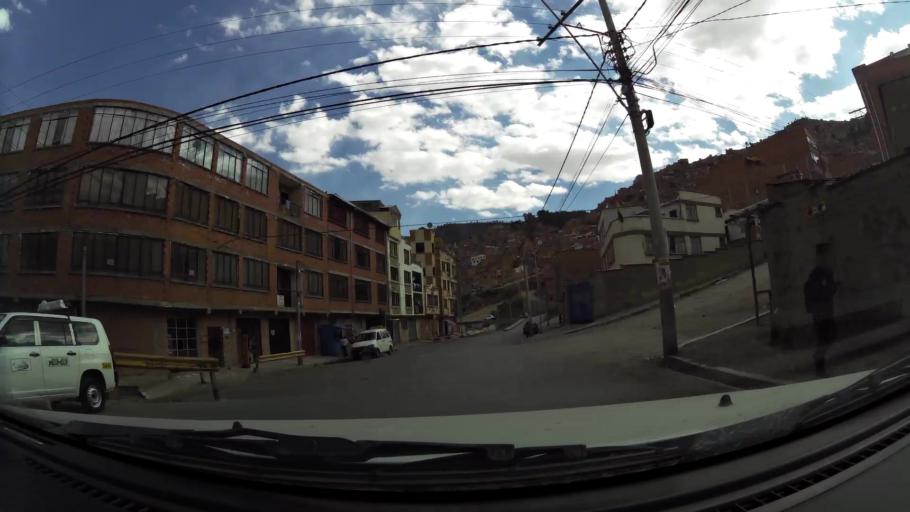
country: BO
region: La Paz
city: La Paz
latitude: -16.4739
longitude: -68.1201
